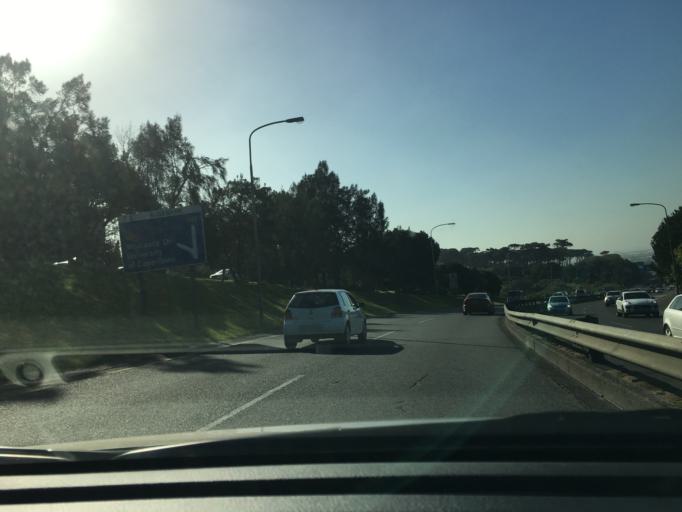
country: ZA
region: Western Cape
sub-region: City of Cape Town
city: Rosebank
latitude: -33.9560
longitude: 18.4638
